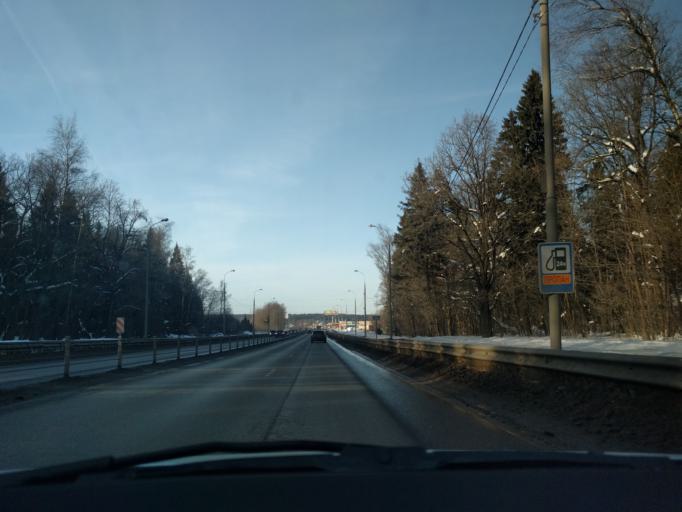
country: RU
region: Moskovskaya
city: Marfino
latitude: 56.0377
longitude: 37.5426
